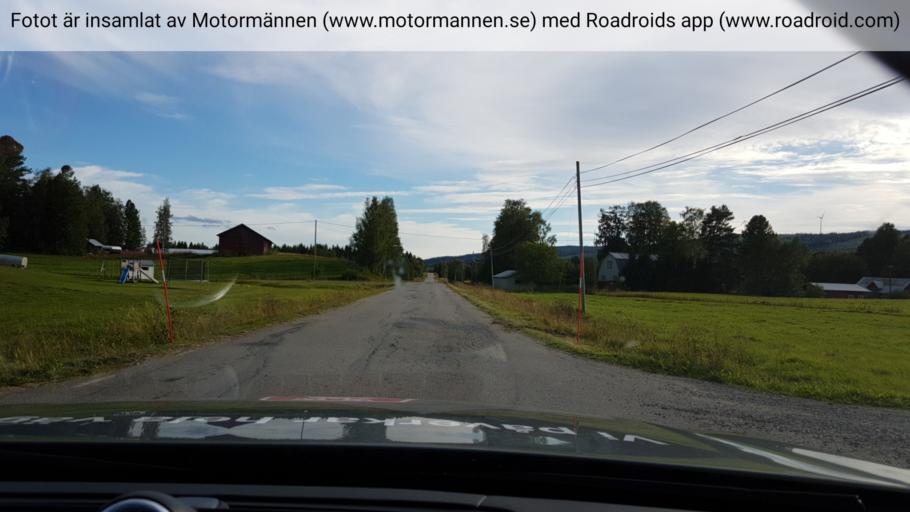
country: SE
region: Jaemtland
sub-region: Stroemsunds Kommun
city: Stroemsund
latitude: 64.0727
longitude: 15.8255
